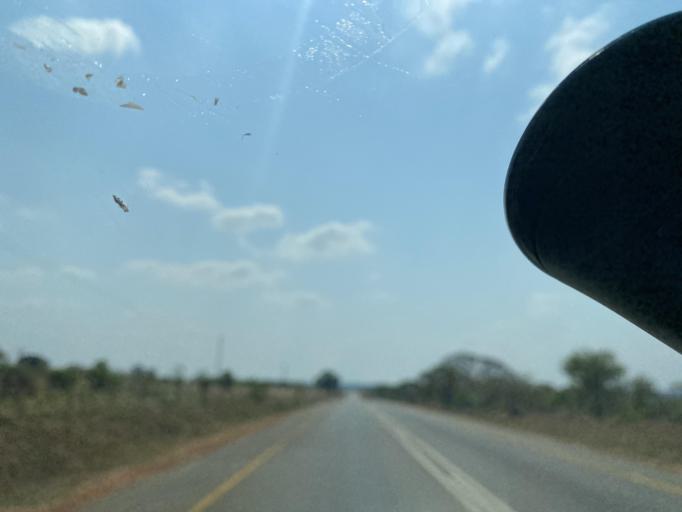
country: ZM
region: Lusaka
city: Chongwe
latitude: -15.5305
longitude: 28.6314
